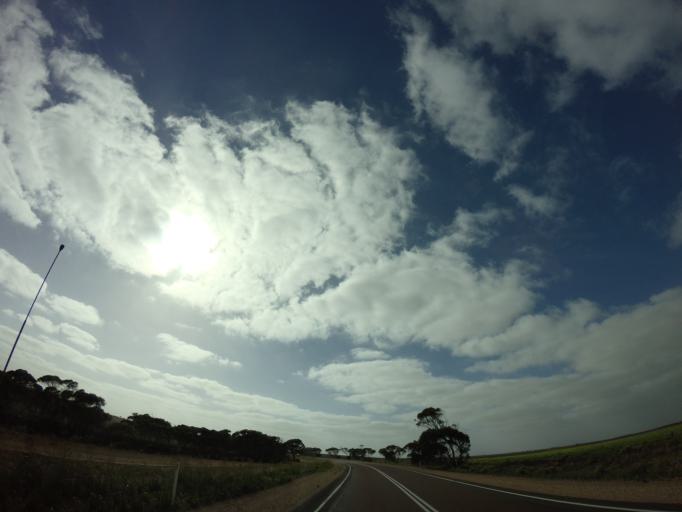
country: AU
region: South Australia
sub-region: Streaky Bay
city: Streaky Bay
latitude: -32.2792
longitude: 134.2189
